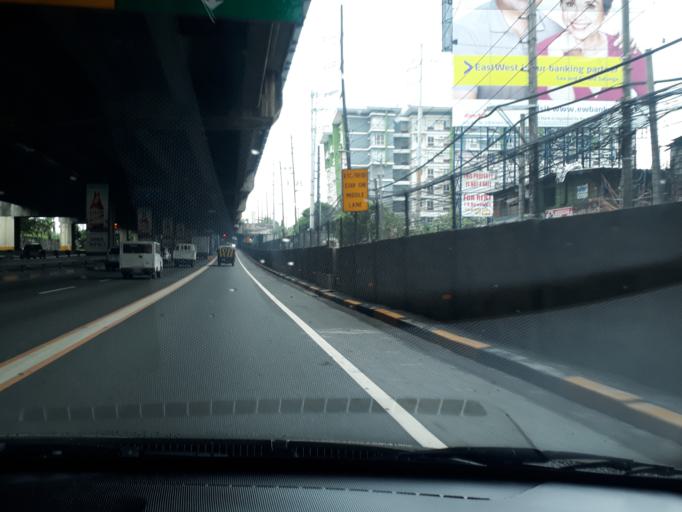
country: PH
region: Calabarzon
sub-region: Province of Rizal
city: Taguig
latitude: 14.4948
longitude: 121.0413
